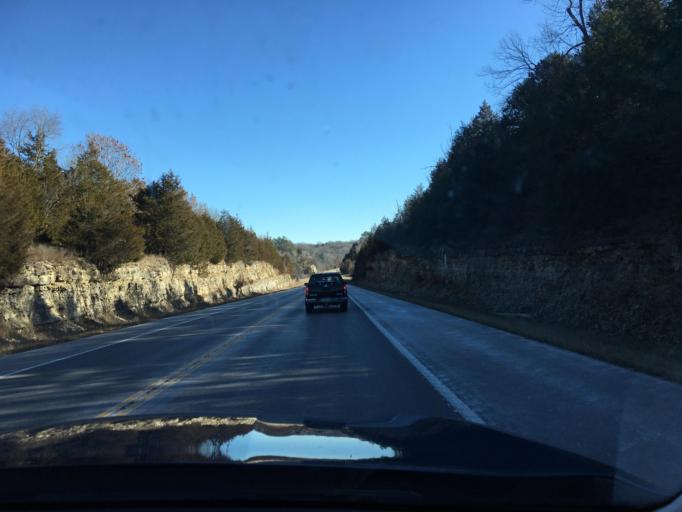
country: US
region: Missouri
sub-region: Jefferson County
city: De Soto
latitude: 38.1384
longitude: -90.4956
